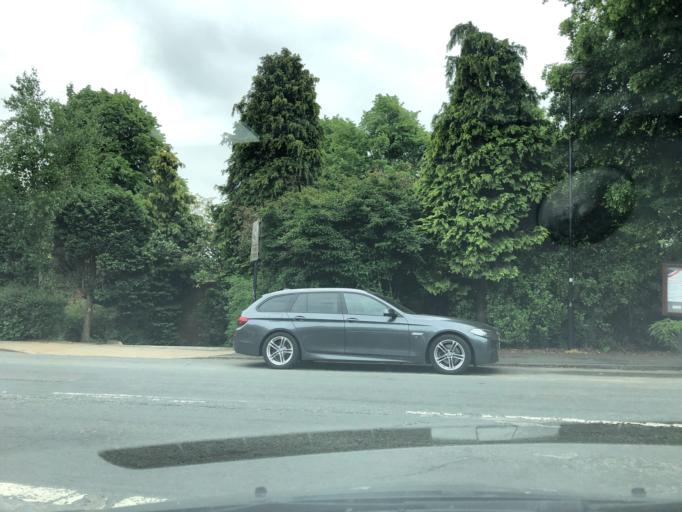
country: GB
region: England
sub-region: North Yorkshire
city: Harrogate
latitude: 53.9935
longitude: -1.5491
